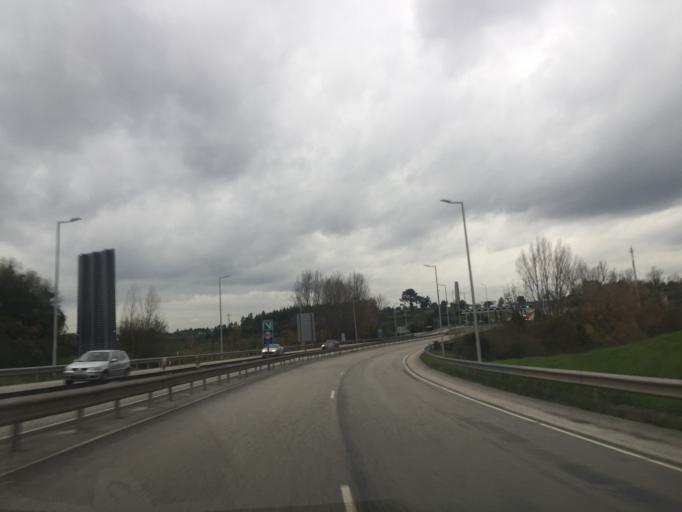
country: PT
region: Coimbra
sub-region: Condeixa-A-Nova
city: Condeixa-a-Nova
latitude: 40.1298
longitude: -8.4895
